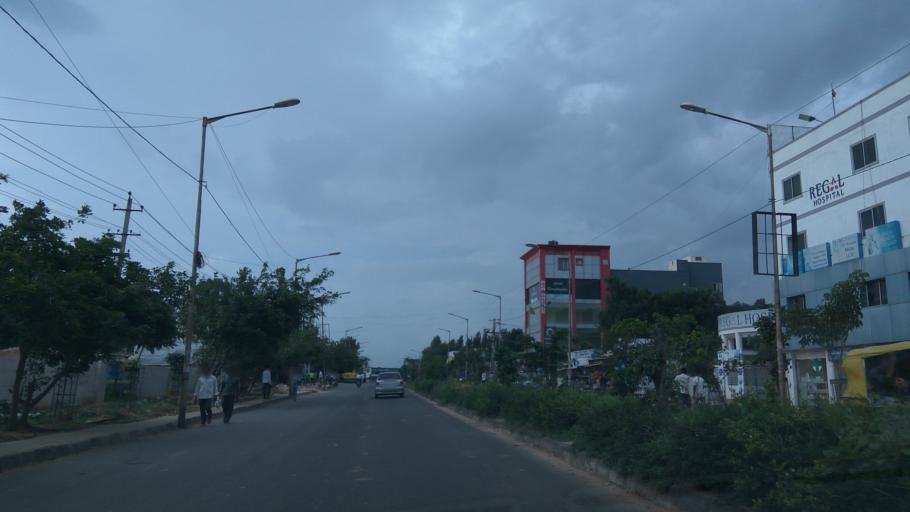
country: IN
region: Karnataka
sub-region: Bangalore Urban
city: Yelahanka
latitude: 13.0832
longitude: 77.6345
